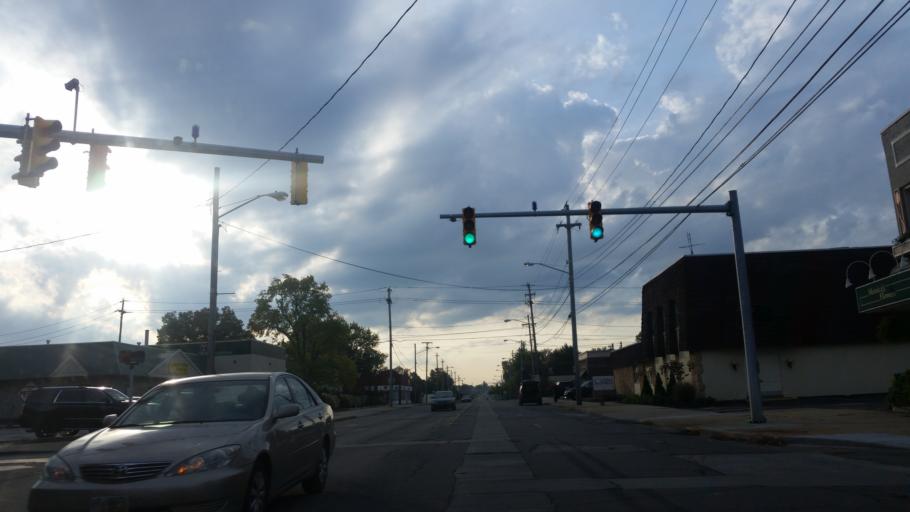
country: US
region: Ohio
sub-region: Cuyahoga County
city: Garfield Heights
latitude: 41.4341
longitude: -81.6187
